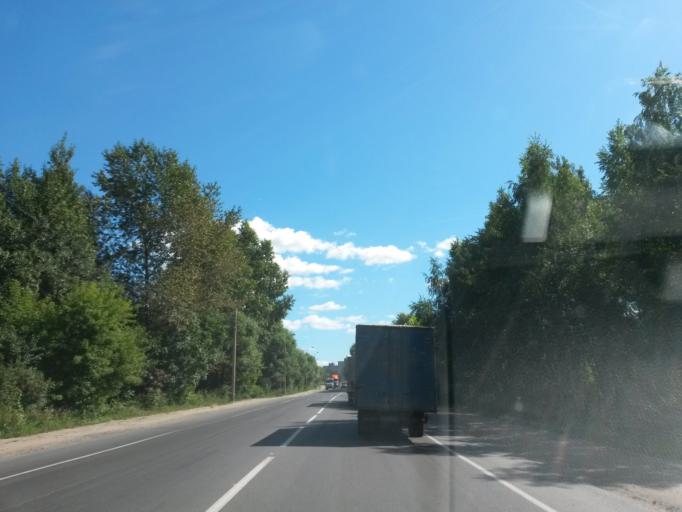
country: RU
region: Jaroslavl
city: Yaroslavl
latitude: 57.5919
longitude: 39.8155
